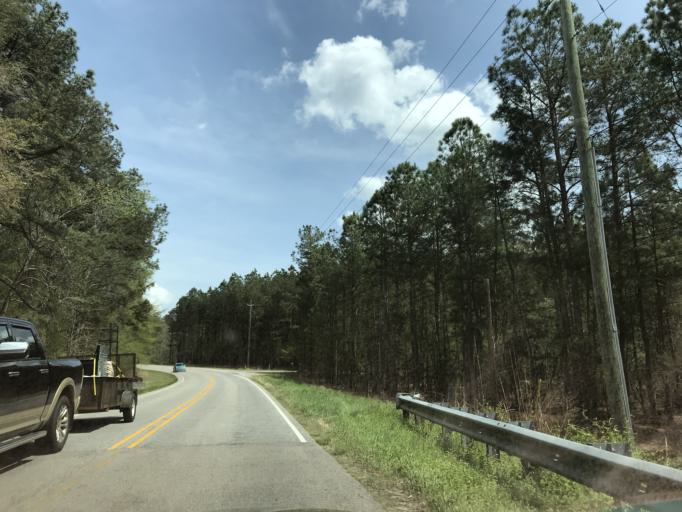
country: US
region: North Carolina
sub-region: Nash County
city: Spring Hope
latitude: 35.9665
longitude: -78.2200
